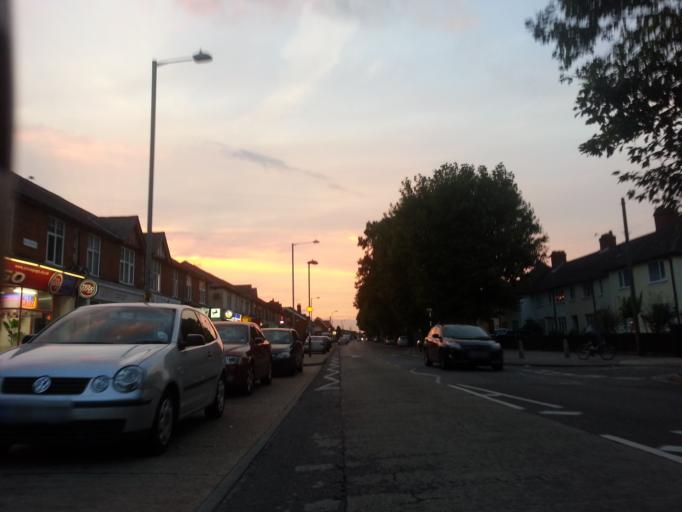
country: GB
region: England
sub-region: Suffolk
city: Ipswich
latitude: 52.0385
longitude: 1.1878
